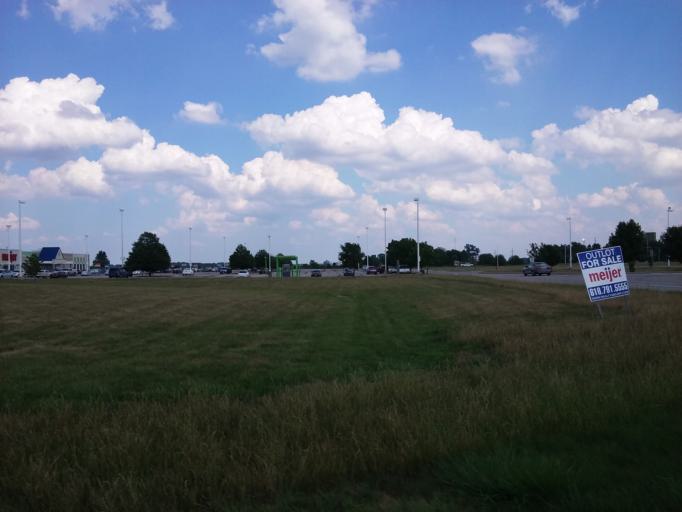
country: US
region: Ohio
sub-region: Wood County
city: Bowling Green
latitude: 41.3757
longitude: -83.6103
